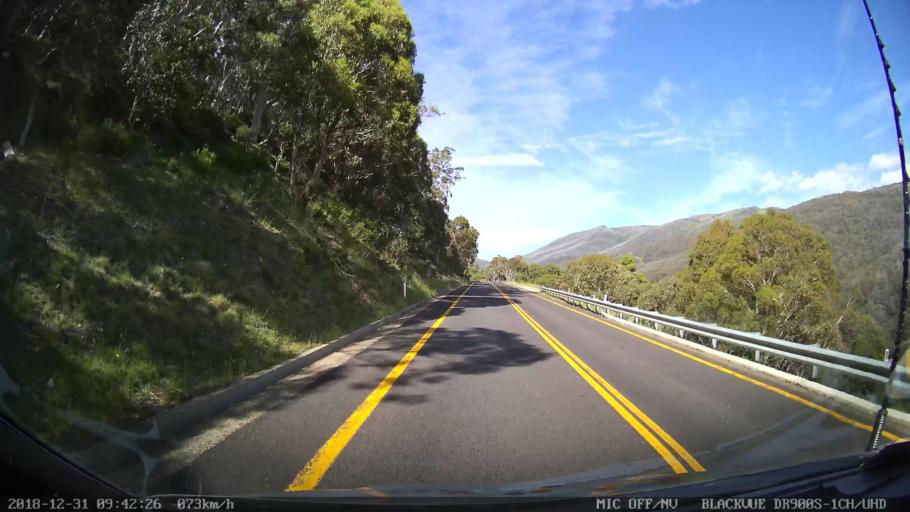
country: AU
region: New South Wales
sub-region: Snowy River
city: Jindabyne
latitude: -36.4964
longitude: 148.3230
